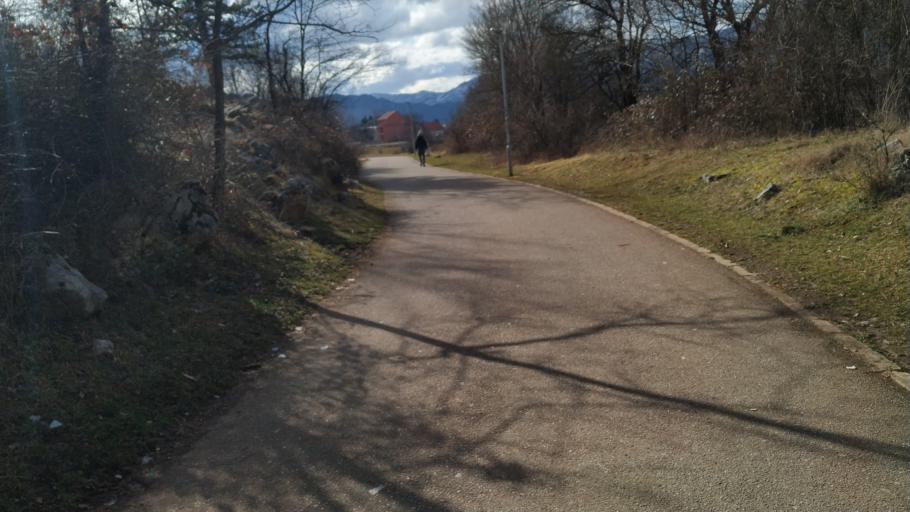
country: ME
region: Opstina Niksic
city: Niksic
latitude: 42.7662
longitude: 18.9560
